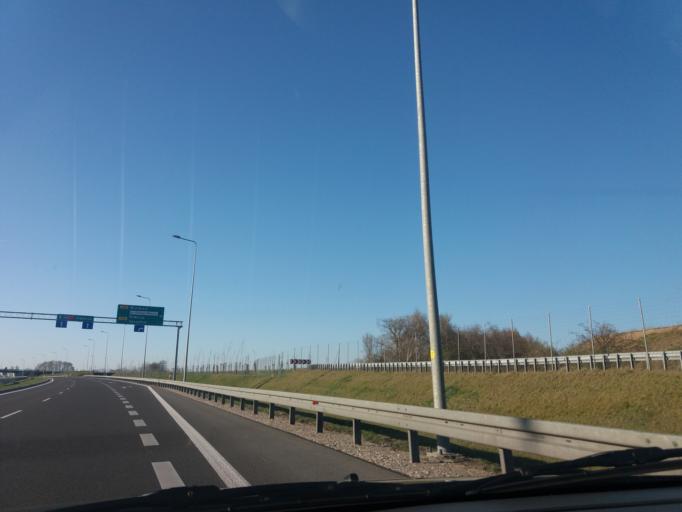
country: PL
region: Warmian-Masurian Voivodeship
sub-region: Powiat nidzicki
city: Nidzica
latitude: 53.3290
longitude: 20.4394
